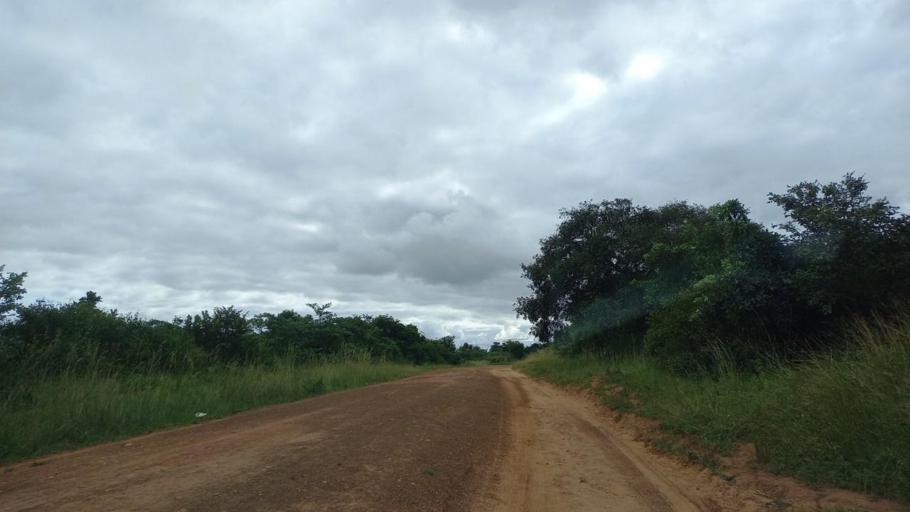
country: ZM
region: Lusaka
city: Chongwe
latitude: -15.4563
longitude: 28.8636
